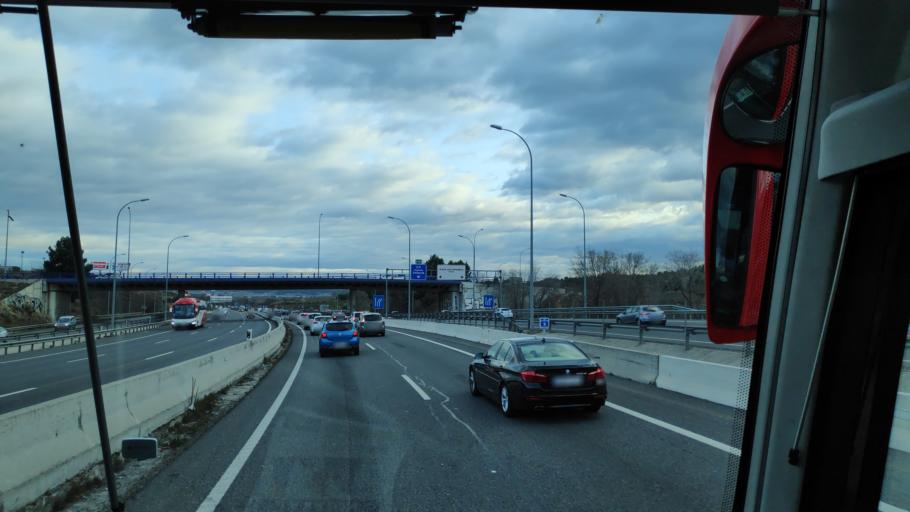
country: ES
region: Madrid
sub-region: Provincia de Madrid
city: Villa de Vallecas
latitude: 40.3544
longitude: -3.5528
